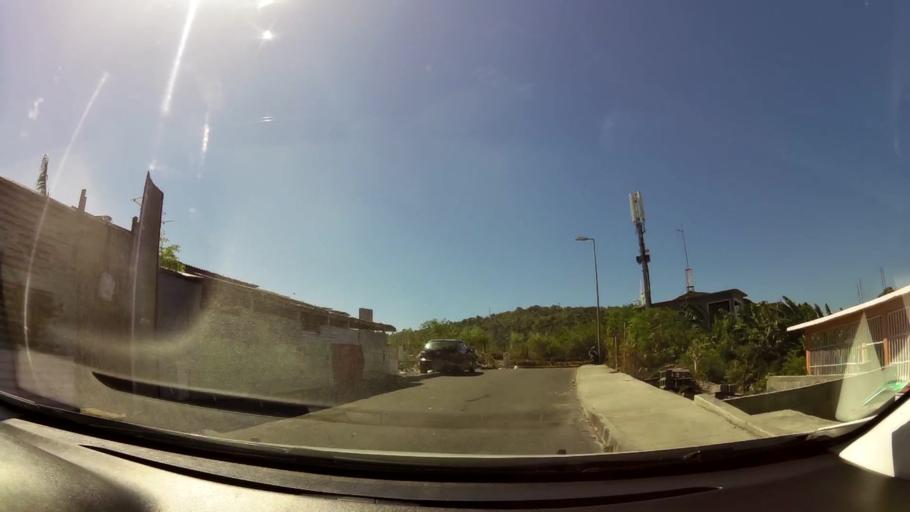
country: YT
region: Pamandzi
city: Pamandzi
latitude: -12.7977
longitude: 45.2793
